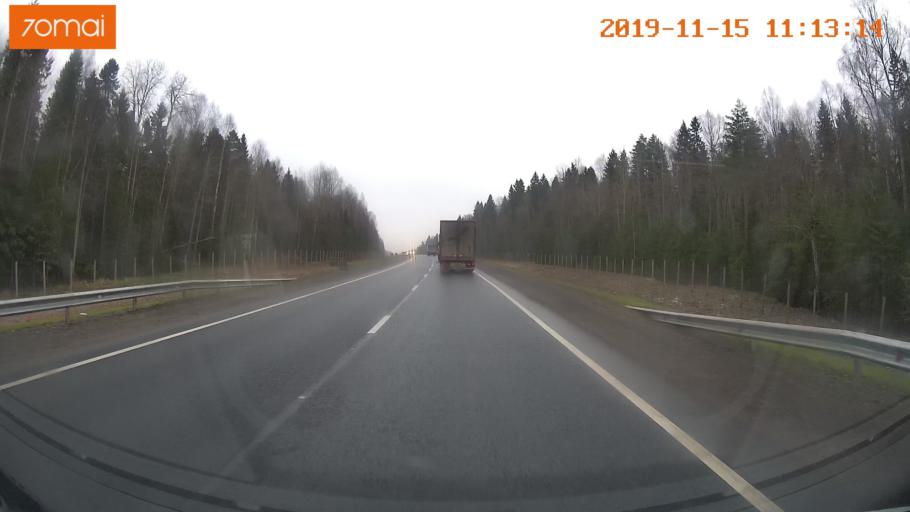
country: RU
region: Vologda
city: Chebsara
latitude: 59.1218
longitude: 39.1645
